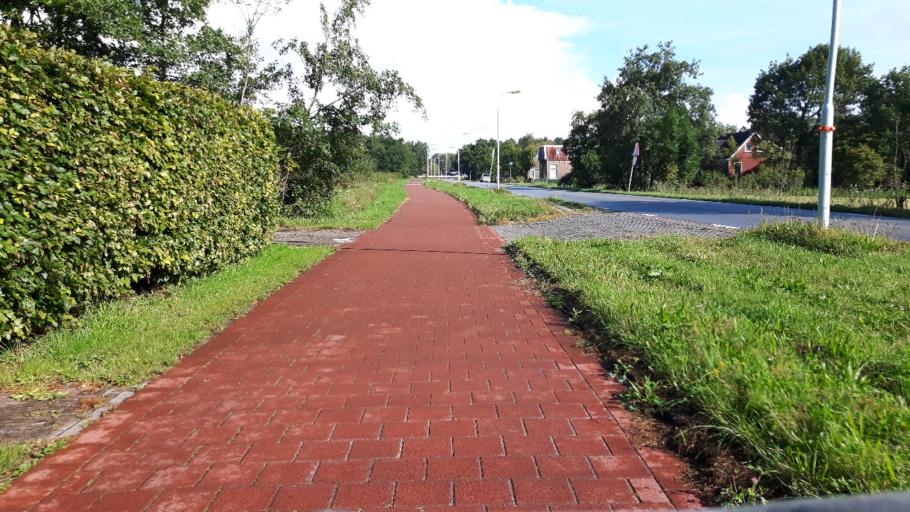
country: NL
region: Friesland
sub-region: Gemeente Smallingerland
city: Drachten
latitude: 53.0894
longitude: 6.0996
